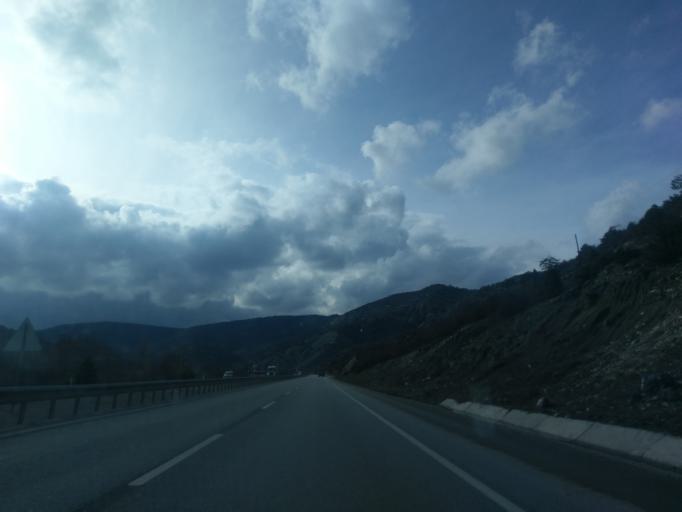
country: TR
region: Kuetahya
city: Sabuncu
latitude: 39.5572
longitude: 30.0719
